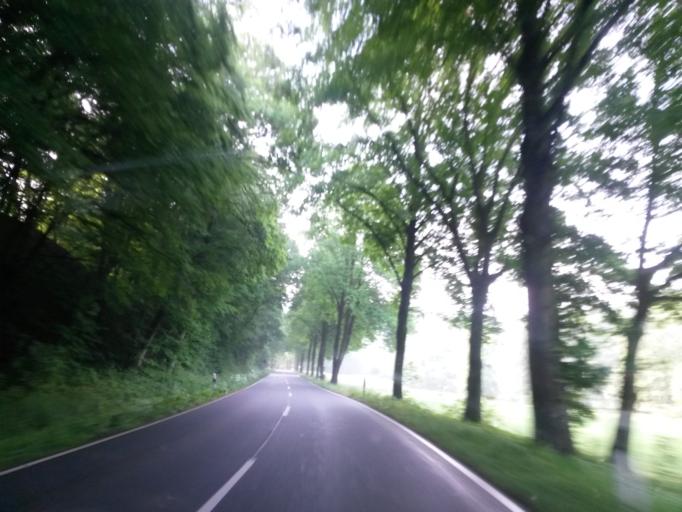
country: DE
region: North Rhine-Westphalia
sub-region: Regierungsbezirk Koln
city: Much
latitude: 50.8779
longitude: 7.3514
